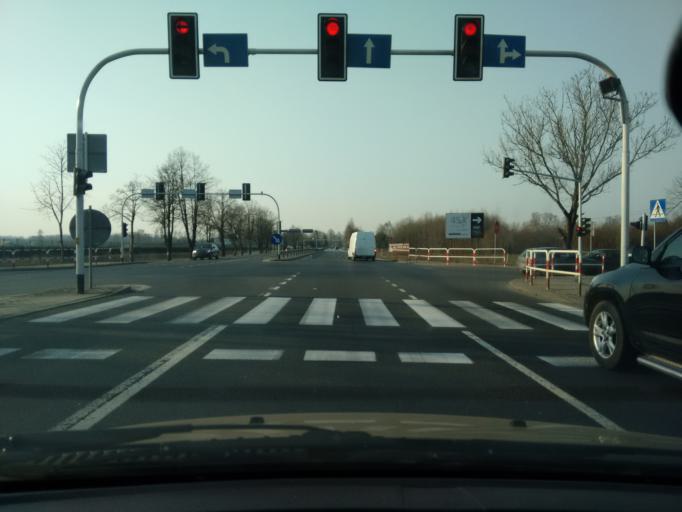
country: PL
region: Silesian Voivodeship
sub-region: Powiat cieszynski
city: Drogomysl
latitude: 49.8678
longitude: 18.7473
